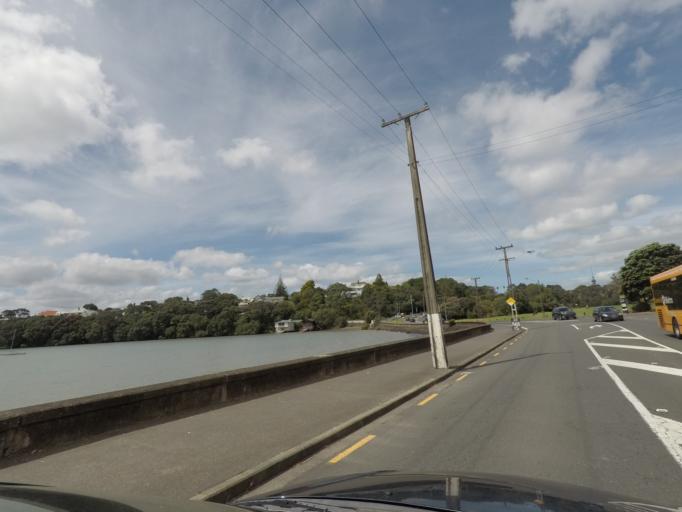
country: NZ
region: Auckland
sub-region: Auckland
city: Auckland
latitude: -36.8516
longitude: 174.7233
